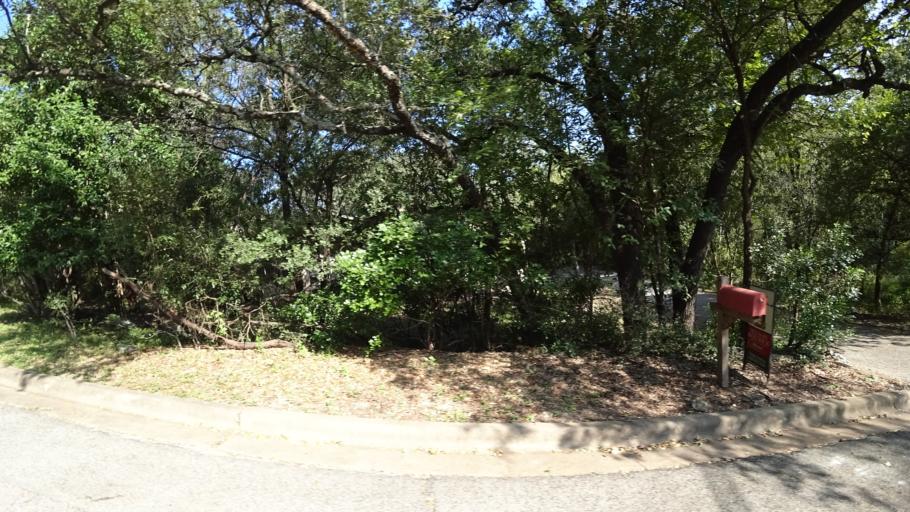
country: US
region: Texas
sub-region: Travis County
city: Rollingwood
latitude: 30.2866
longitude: -97.7956
